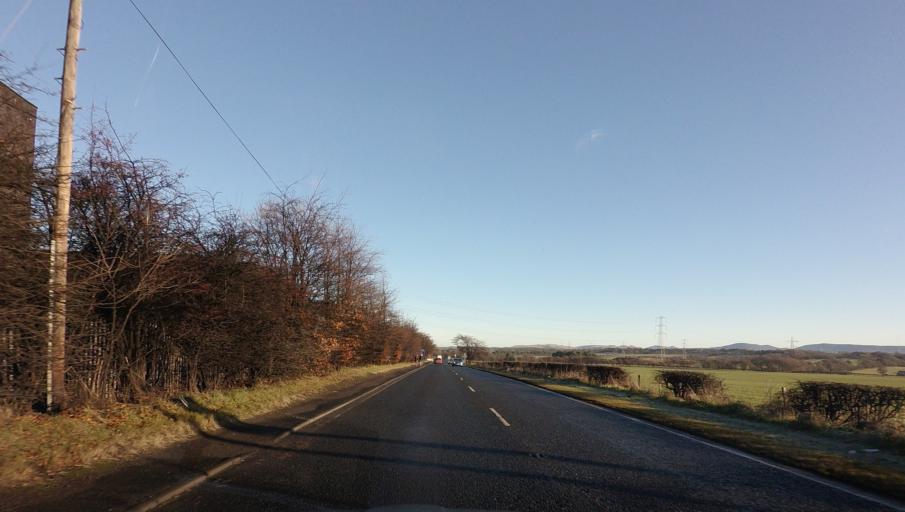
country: GB
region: Scotland
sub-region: West Lothian
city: Blackburn
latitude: 55.8403
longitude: -3.6070
